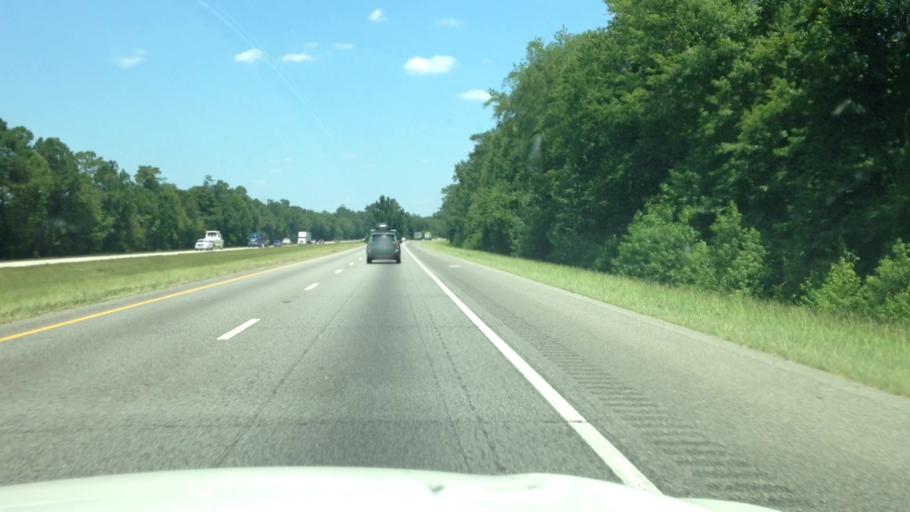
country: US
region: South Carolina
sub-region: Dillon County
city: Latta
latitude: 34.3984
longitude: -79.4512
